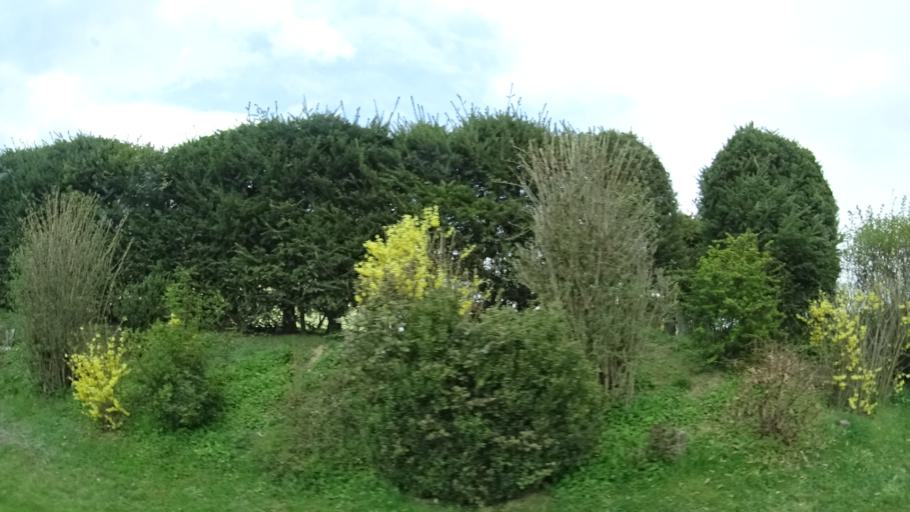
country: DE
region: Rheinland-Pfalz
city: Heinzenberg
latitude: 49.8106
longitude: 7.4811
